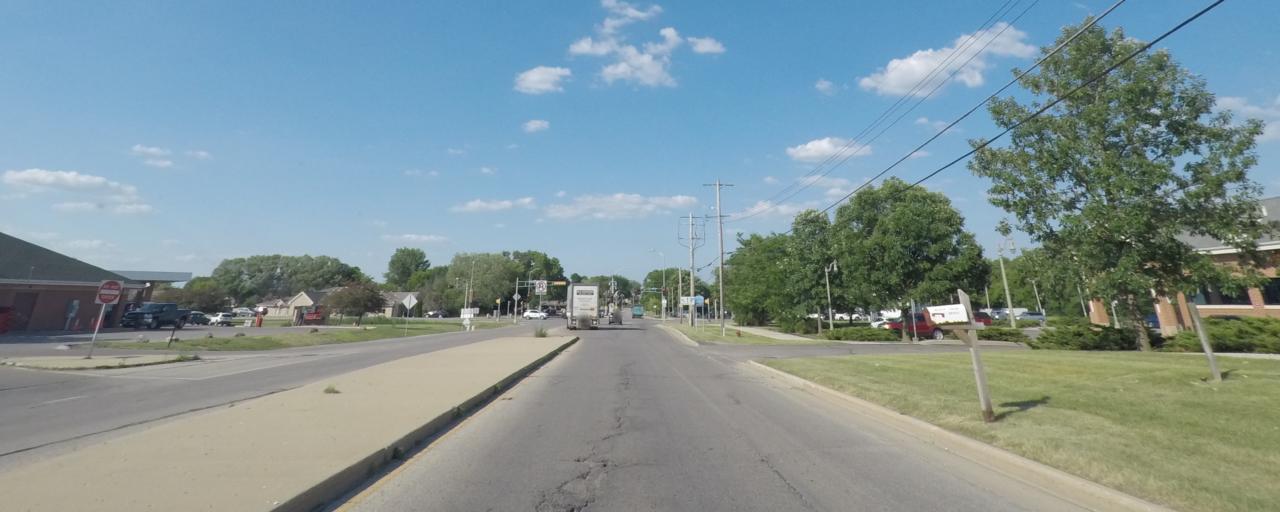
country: US
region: Wisconsin
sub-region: Waukesha County
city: Muskego
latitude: 42.9008
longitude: -88.1504
